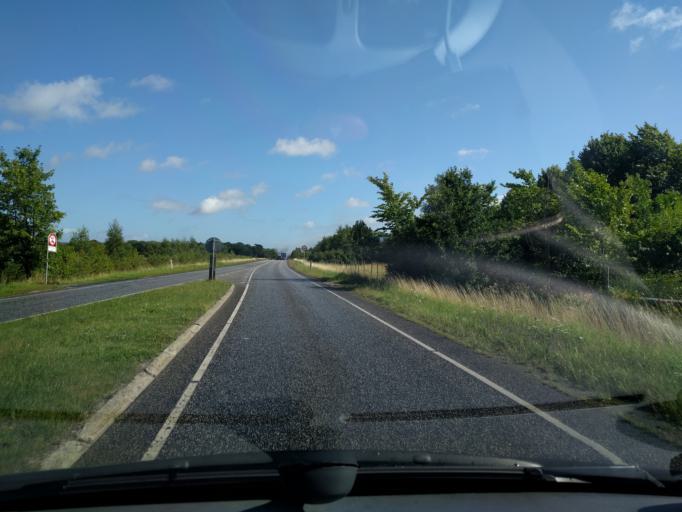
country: DK
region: South Denmark
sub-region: Kerteminde Kommune
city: Langeskov
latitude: 55.3598
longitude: 10.5693
